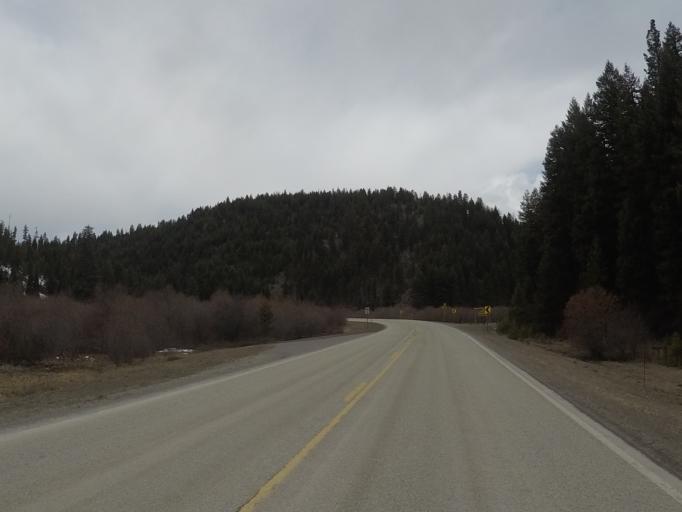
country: US
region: Montana
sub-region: Missoula County
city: Frenchtown
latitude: 46.7819
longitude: -114.3963
